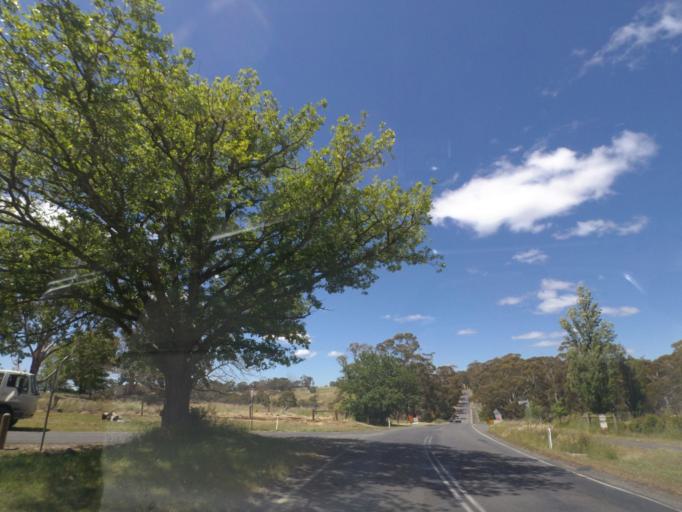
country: AU
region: Victoria
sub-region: Mount Alexander
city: Castlemaine
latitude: -37.2933
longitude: 144.2453
